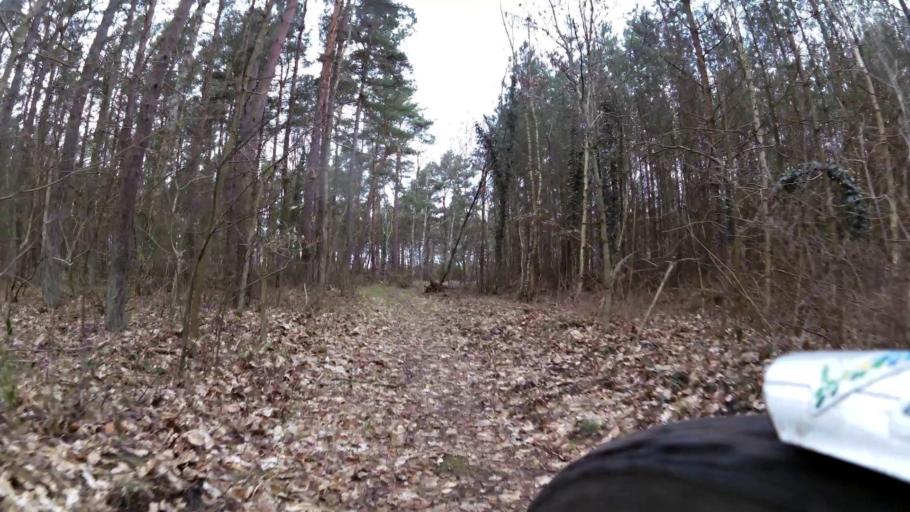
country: PL
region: West Pomeranian Voivodeship
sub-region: Powiat kamienski
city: Dziwnow
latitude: 54.0316
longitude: 14.7794
